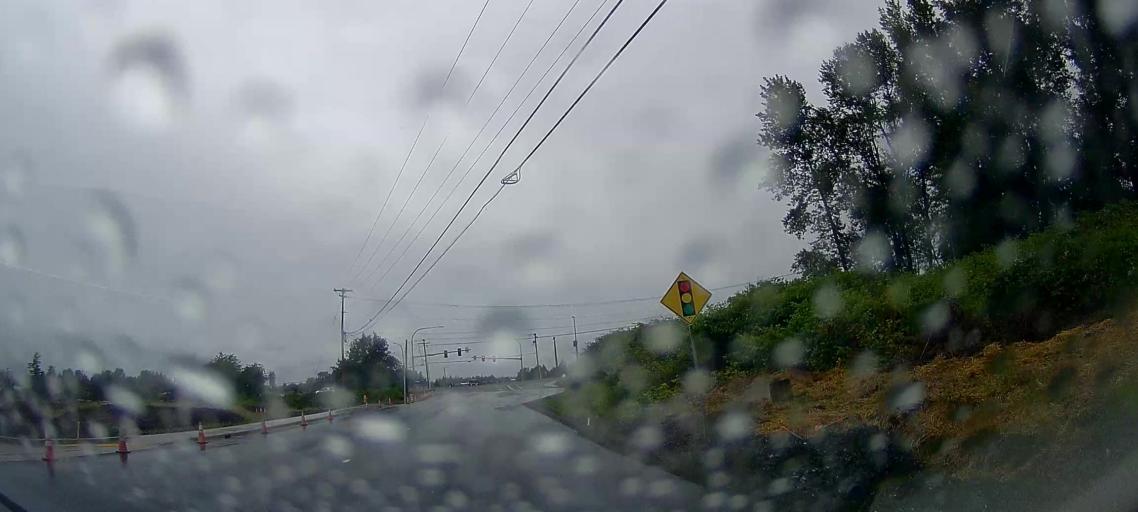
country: US
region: Washington
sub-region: Whatcom County
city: Marietta-Alderwood
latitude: 48.8164
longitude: -122.5547
